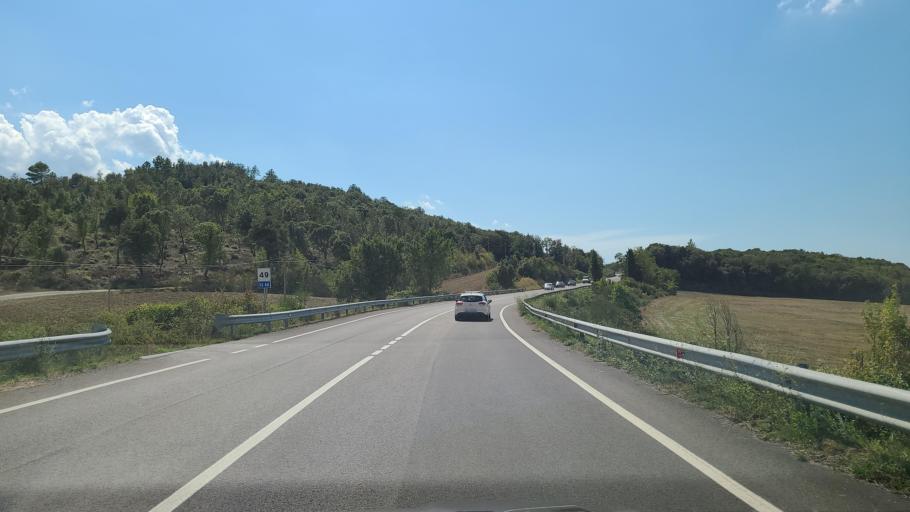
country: IT
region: Tuscany
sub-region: Province of Pisa
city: Volterra
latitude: 43.3966
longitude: 10.9605
